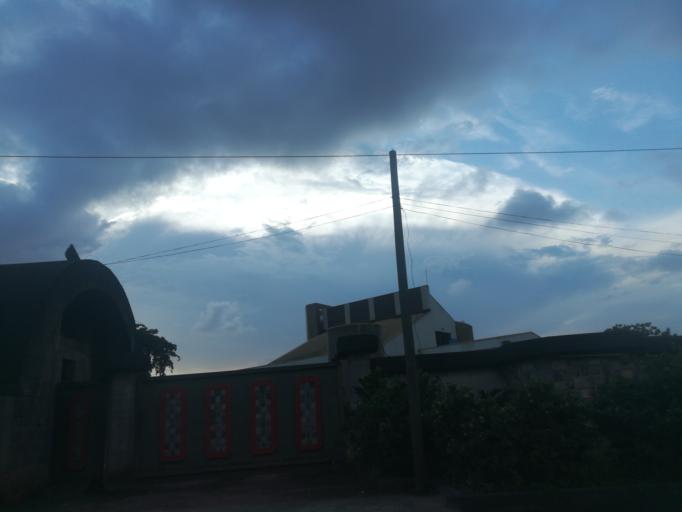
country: NG
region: Lagos
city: Ojota
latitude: 6.5650
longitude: 3.3687
